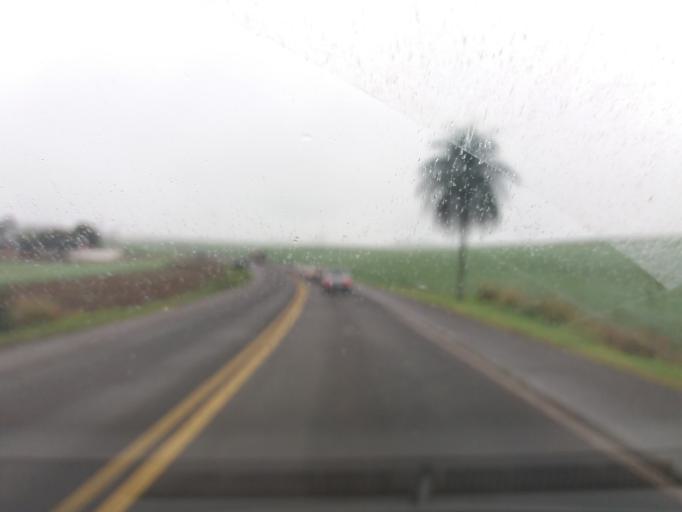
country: BR
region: Parana
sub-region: Realeza
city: Realeza
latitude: -25.8179
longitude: -53.5191
